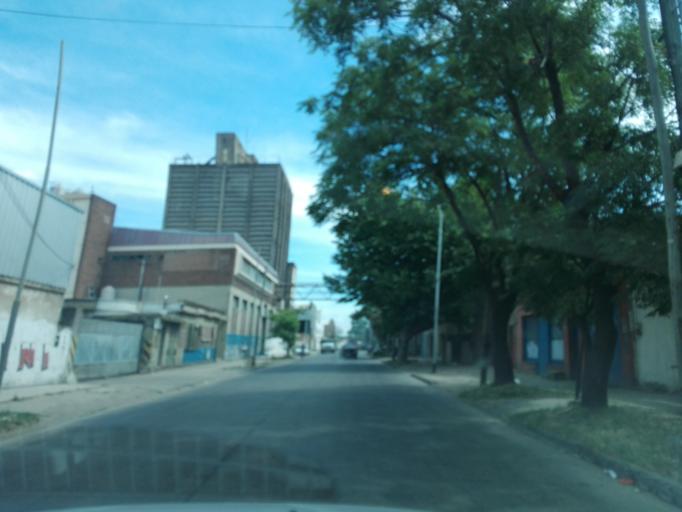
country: AR
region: Buenos Aires
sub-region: Partido de Lanus
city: Lanus
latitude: -34.6969
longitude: -58.3604
